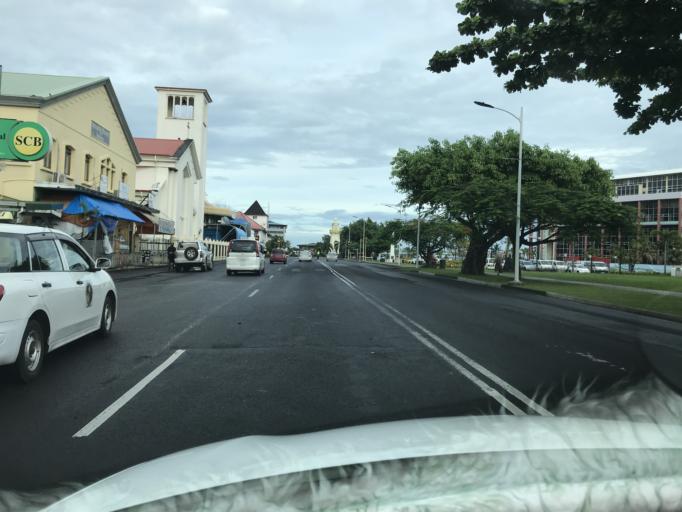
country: WS
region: Tuamasaga
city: Apia
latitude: -13.8314
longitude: -171.7667
